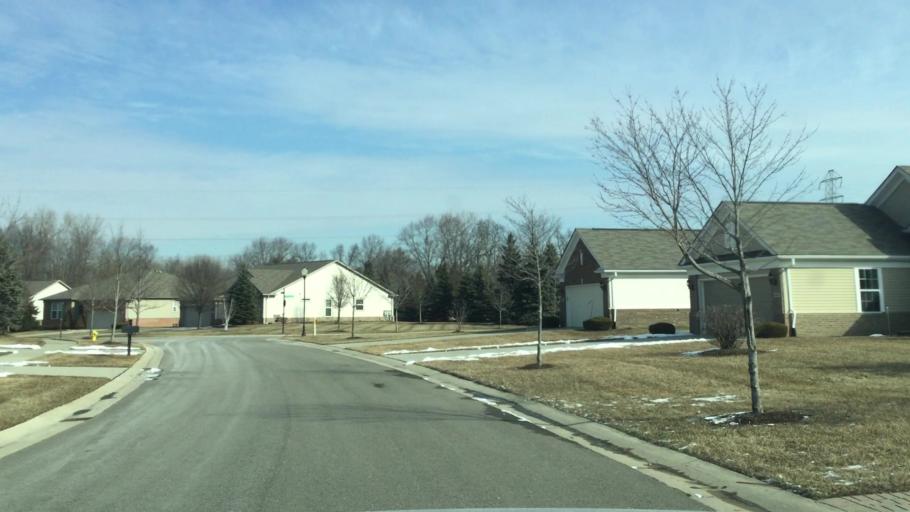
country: US
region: Michigan
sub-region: Wayne County
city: Flat Rock
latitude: 42.1324
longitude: -83.2912
